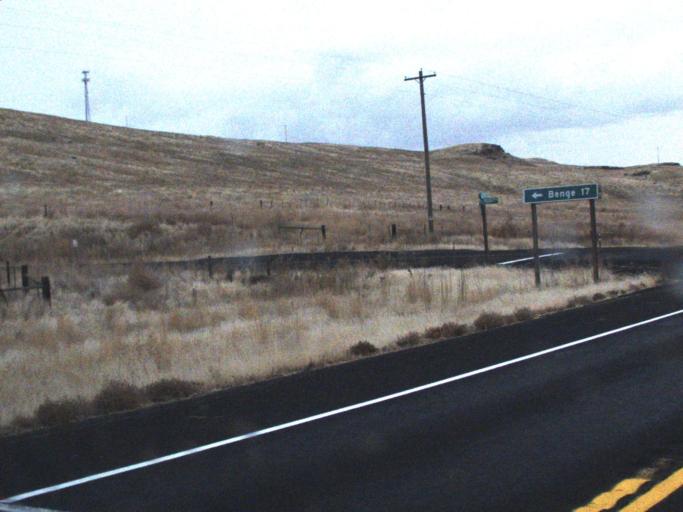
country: US
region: Washington
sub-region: Adams County
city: Ritzville
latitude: 46.7786
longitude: -118.0833
